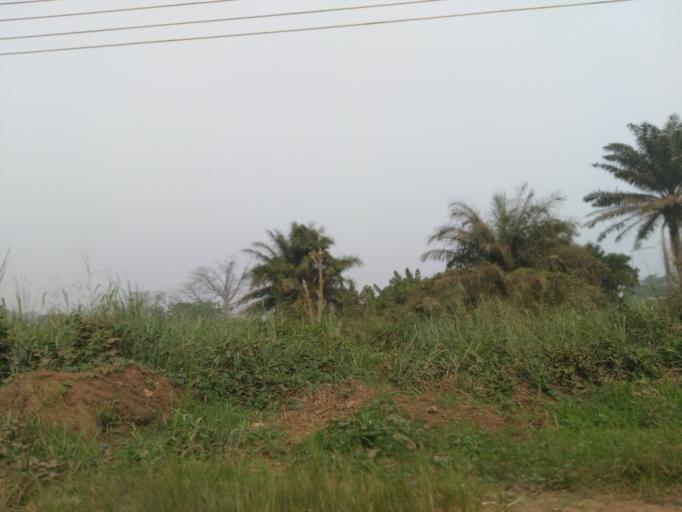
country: GH
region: Ashanti
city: Kumasi
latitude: 6.6526
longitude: -1.6219
